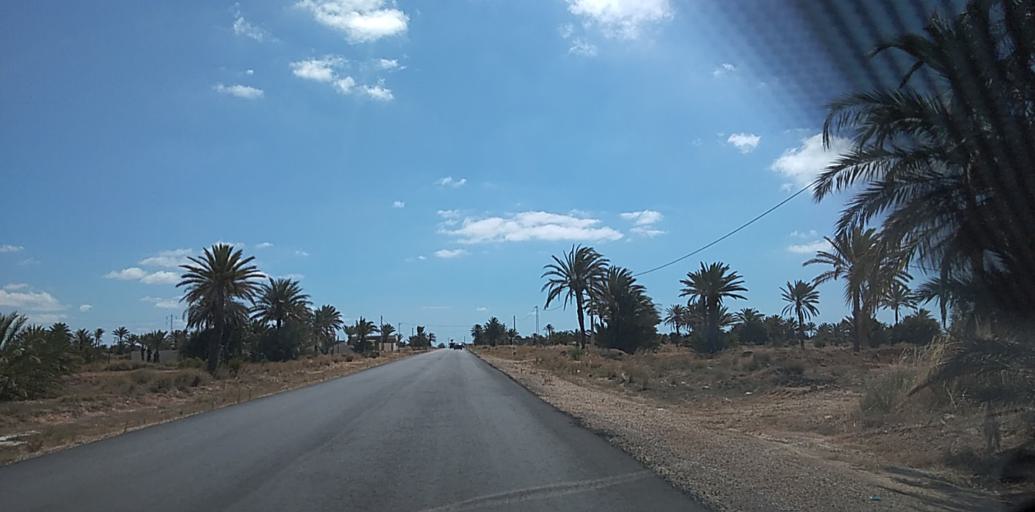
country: TN
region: Safaqis
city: Al Qarmadah
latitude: 34.6597
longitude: 11.1136
